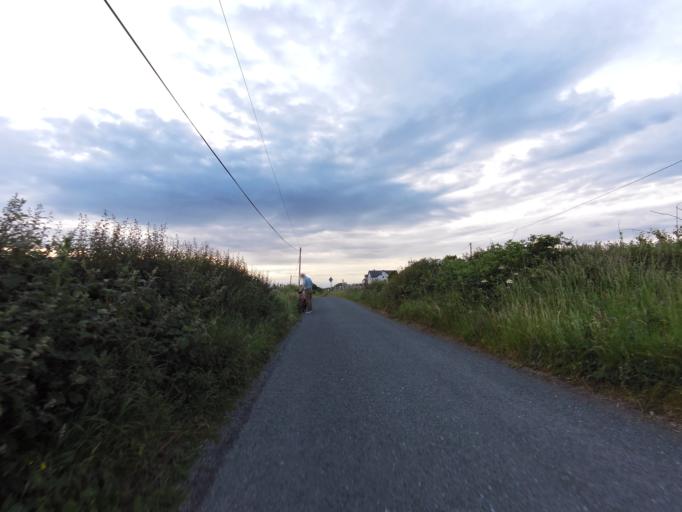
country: IE
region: Connaught
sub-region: County Galway
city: Athenry
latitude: 53.2916
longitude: -8.7188
